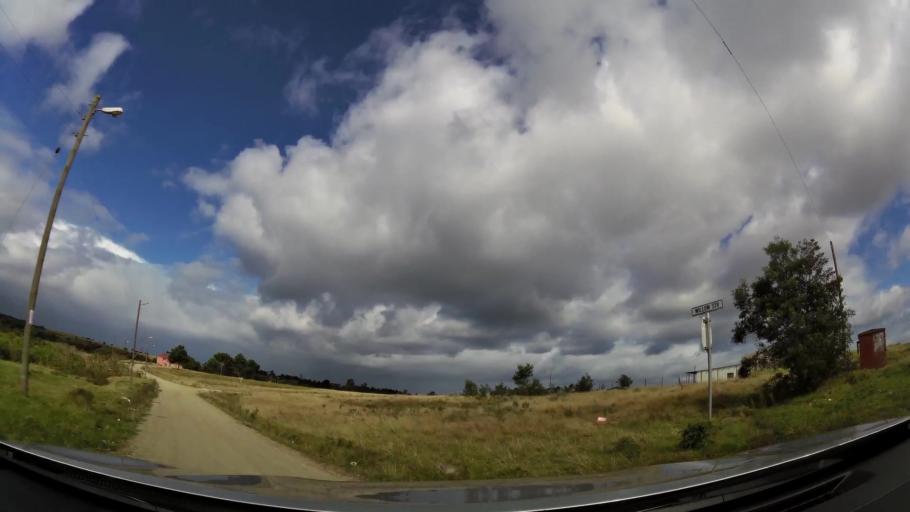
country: ZA
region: Western Cape
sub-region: Eden District Municipality
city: George
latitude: -34.0242
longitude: 22.4681
